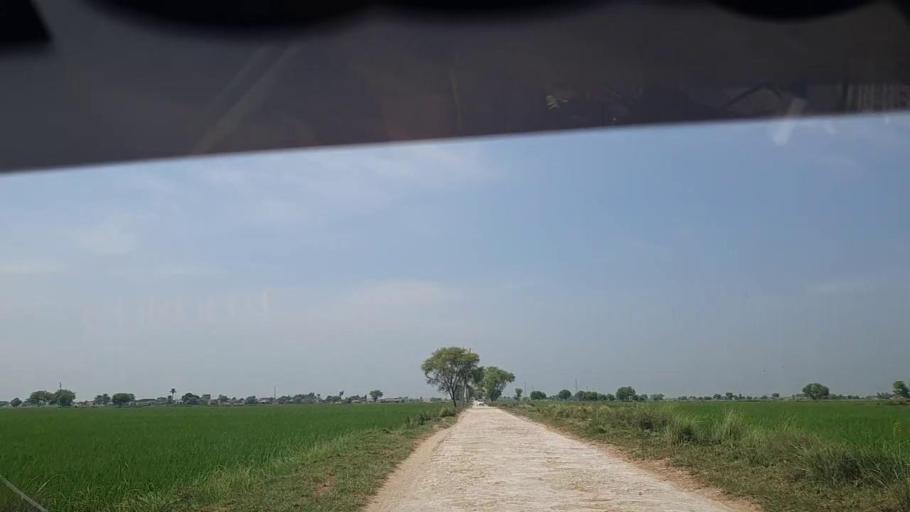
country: PK
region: Sindh
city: Thul
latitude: 28.1731
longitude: 68.7465
